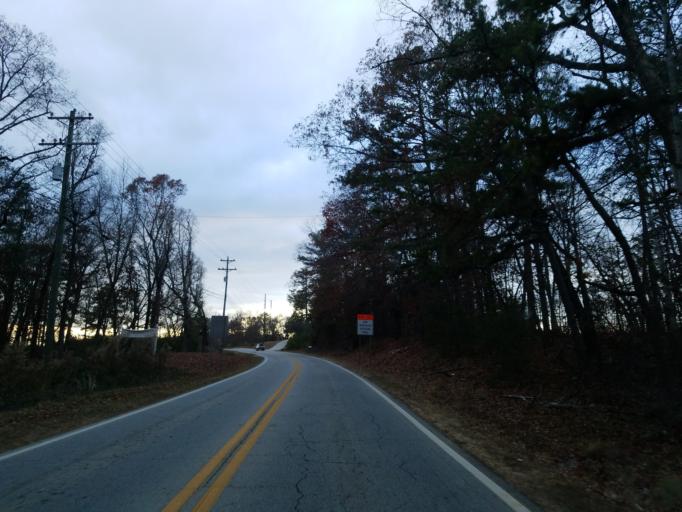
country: US
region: Georgia
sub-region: Dawson County
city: Dawsonville
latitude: 34.3650
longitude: -84.0444
